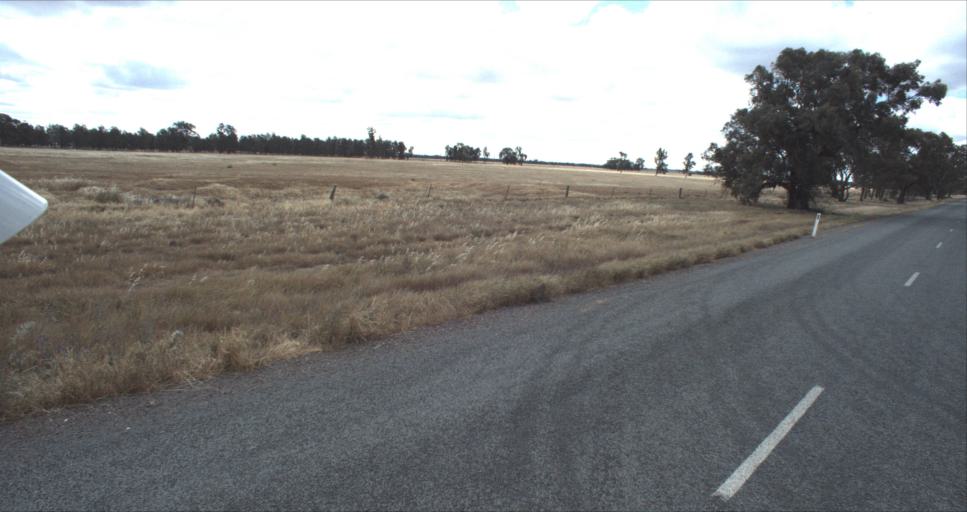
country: AU
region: New South Wales
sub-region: Leeton
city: Leeton
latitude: -34.6864
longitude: 146.3446
